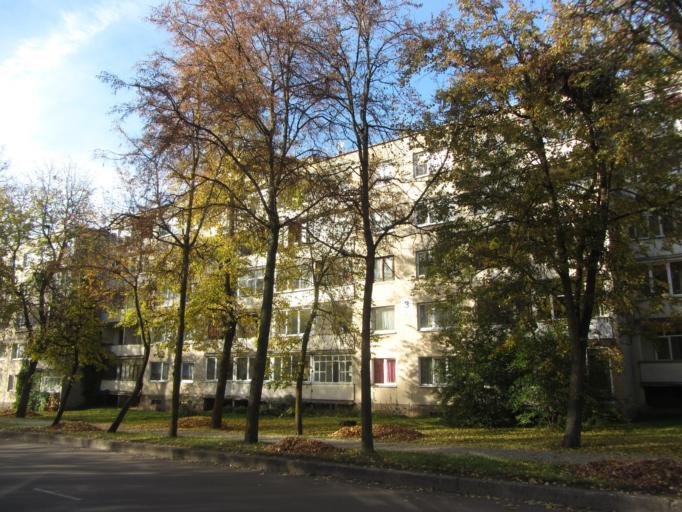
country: LT
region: Vilnius County
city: Elektrenai
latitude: 54.7869
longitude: 24.6605
